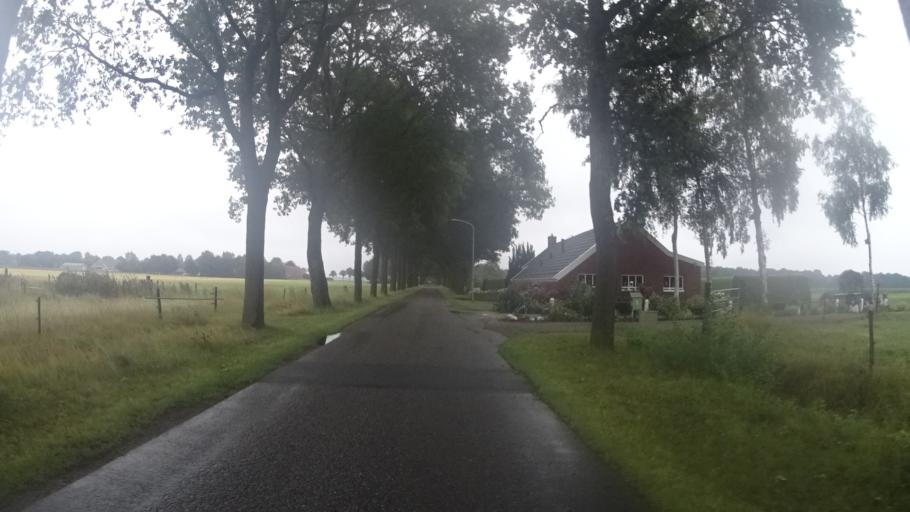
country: NL
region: Groningen
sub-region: Gemeente Veendam
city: Veendam
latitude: 53.1791
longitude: 6.8664
